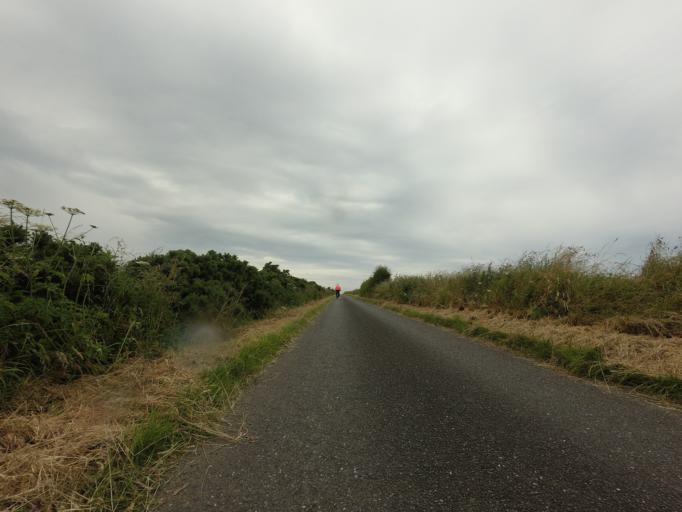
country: GB
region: Scotland
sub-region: Aberdeenshire
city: Portsoy
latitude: 57.6781
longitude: -2.6713
